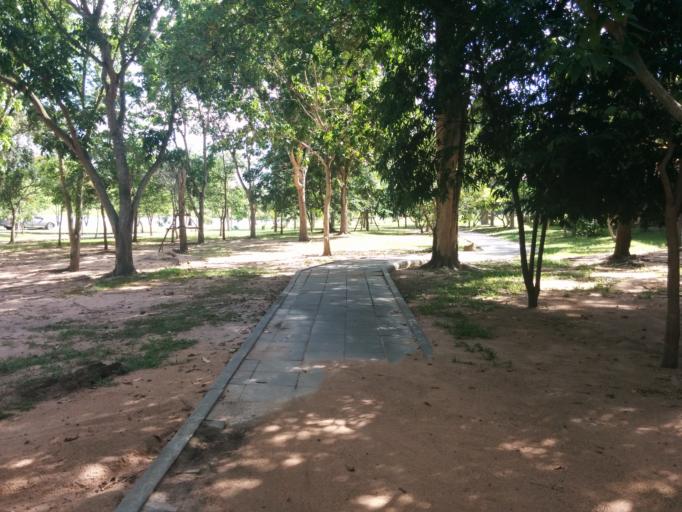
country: TH
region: Chon Buri
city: Phatthaya
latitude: 12.9173
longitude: 100.9953
